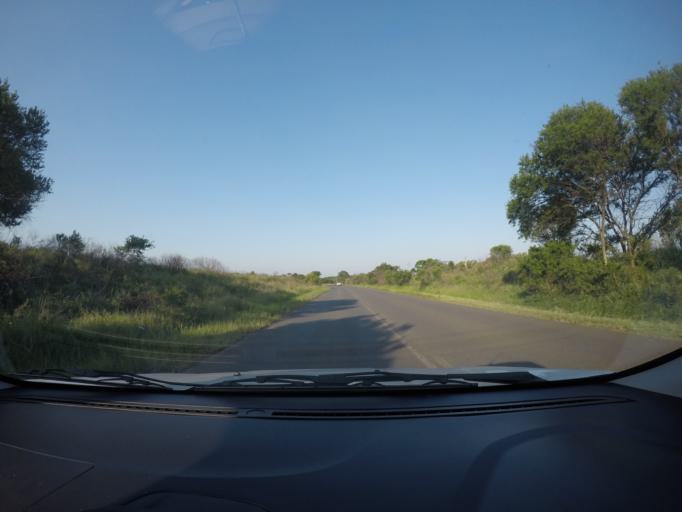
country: ZA
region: KwaZulu-Natal
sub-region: uThungulu District Municipality
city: Richards Bay
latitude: -28.7530
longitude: 32.0088
